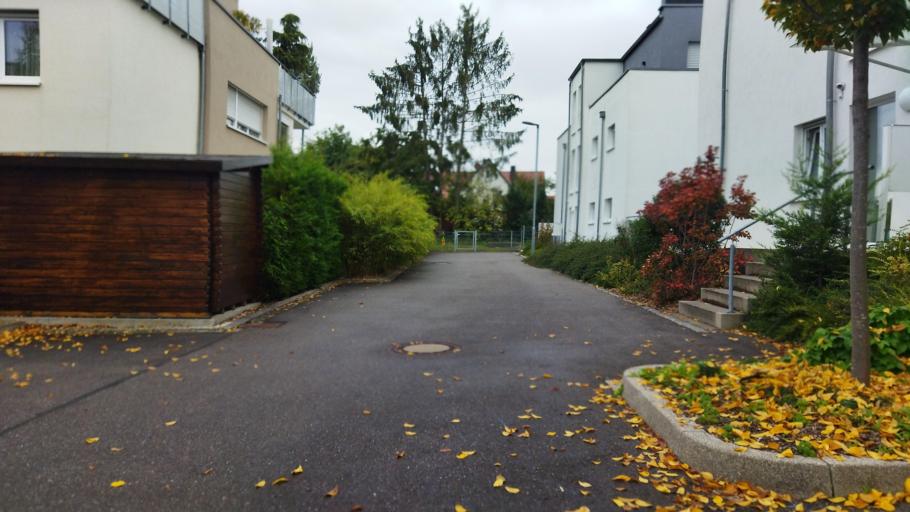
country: DE
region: Baden-Wuerttemberg
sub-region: Regierungsbezirk Stuttgart
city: Heilbronn
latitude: 49.1460
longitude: 9.1910
